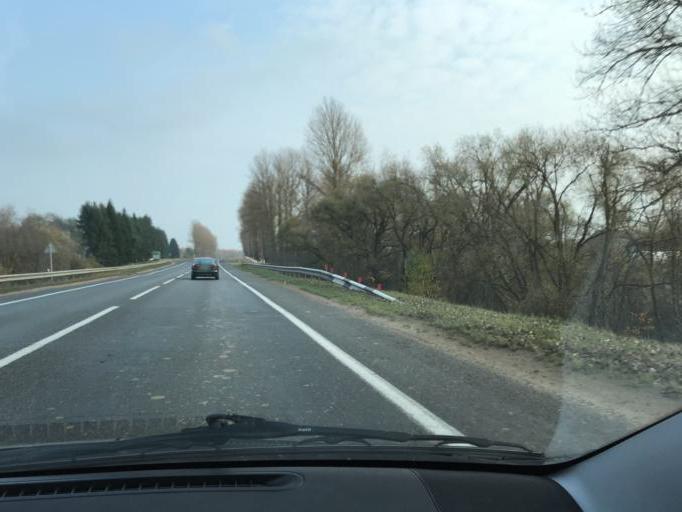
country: BY
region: Vitebsk
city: Vitebsk
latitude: 55.1556
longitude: 29.9734
